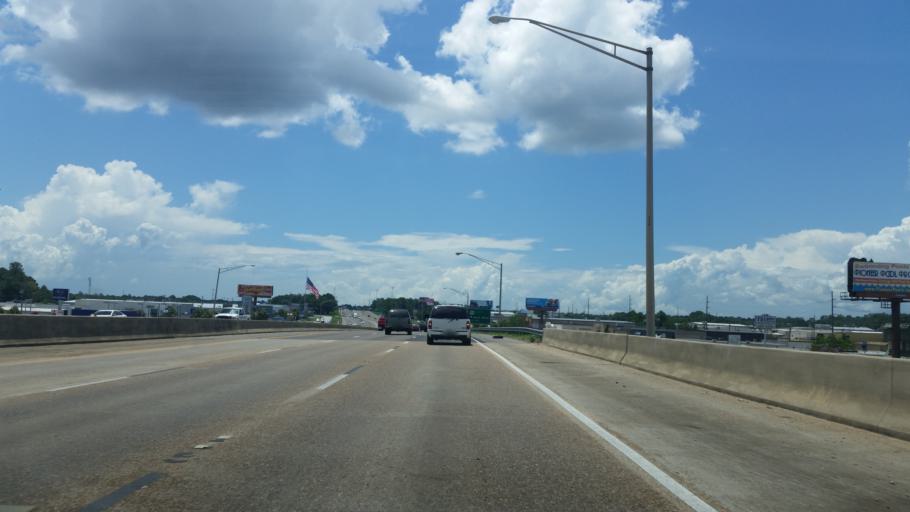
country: US
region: Alabama
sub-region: Mobile County
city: Tillmans Corner
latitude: 30.6617
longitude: -88.1265
